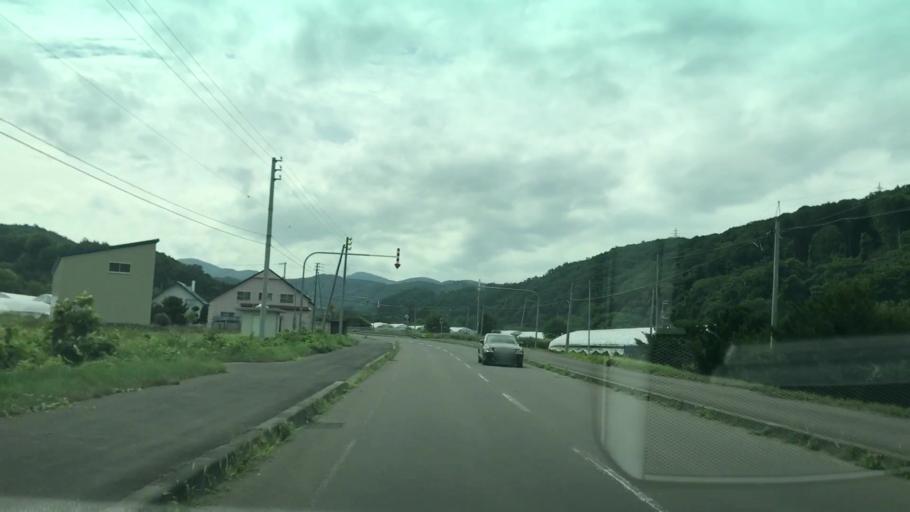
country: JP
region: Hokkaido
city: Yoichi
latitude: 43.1787
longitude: 140.8455
